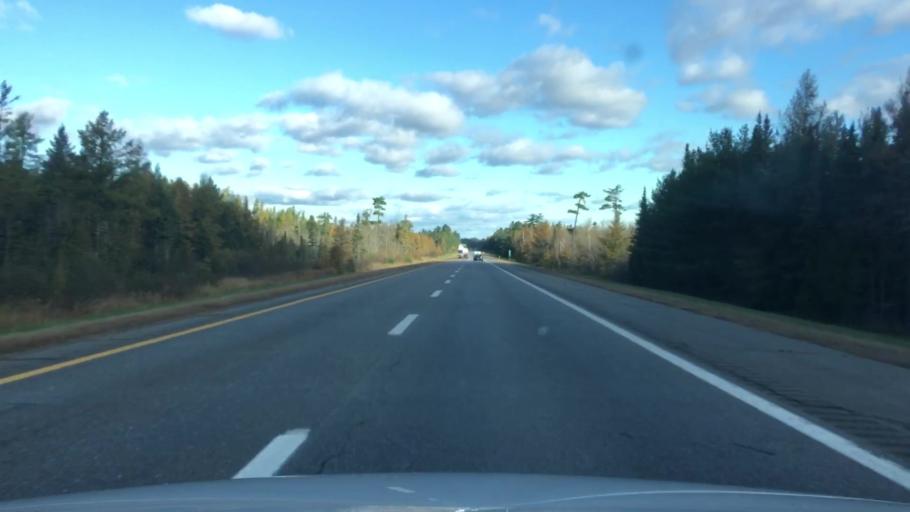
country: US
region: Maine
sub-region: Penobscot County
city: Greenbush
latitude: 45.1292
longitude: -68.6963
